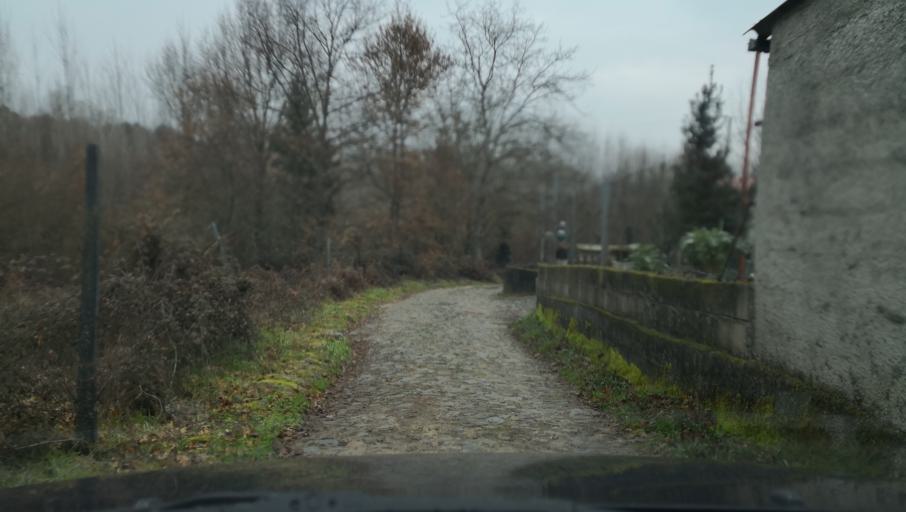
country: PT
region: Vila Real
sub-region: Vila Real
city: Vila Real
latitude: 41.3013
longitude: -7.7743
